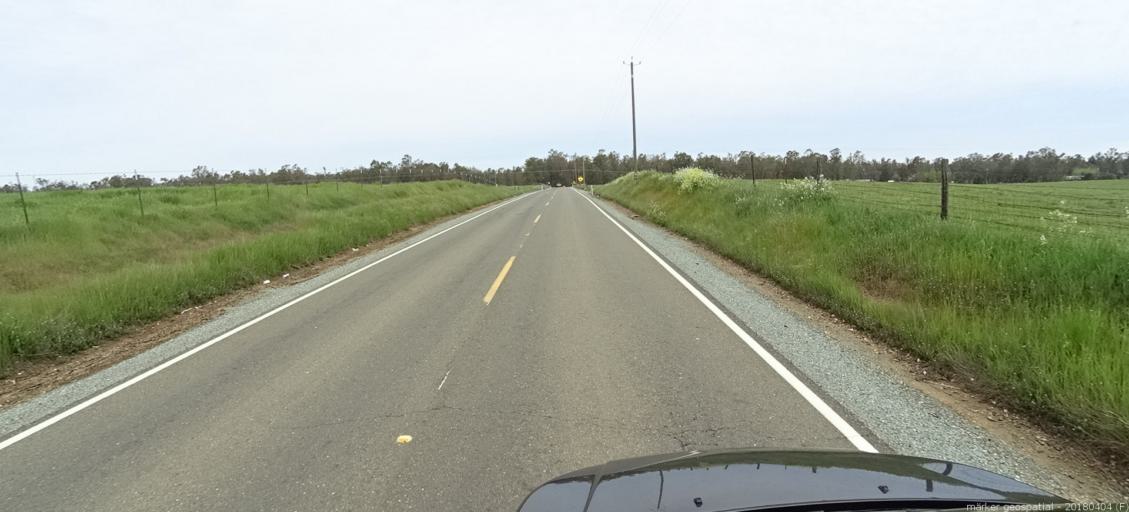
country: US
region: California
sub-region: Sacramento County
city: Clay
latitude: 38.2898
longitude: -121.1713
